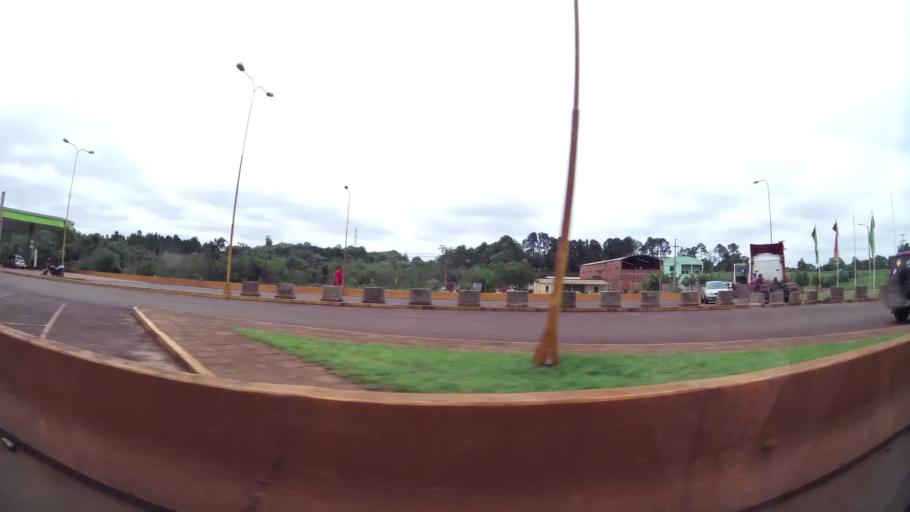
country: PY
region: Alto Parana
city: Ciudad del Este
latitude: -25.4939
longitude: -54.7130
